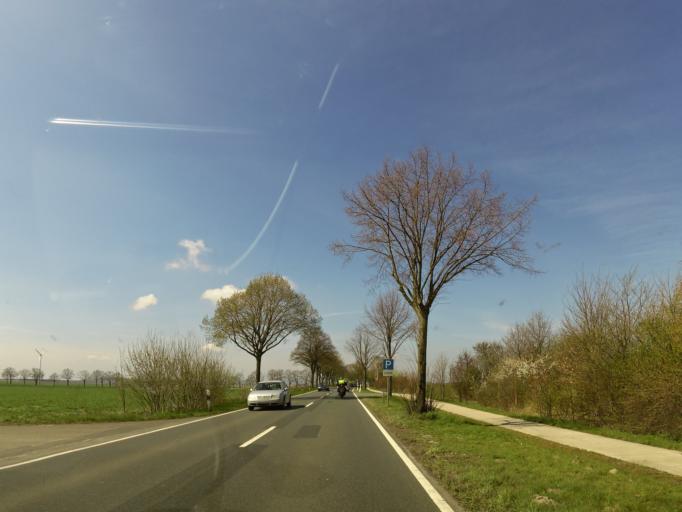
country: DE
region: Lower Saxony
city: Haste
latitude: 52.4331
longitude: 9.3791
